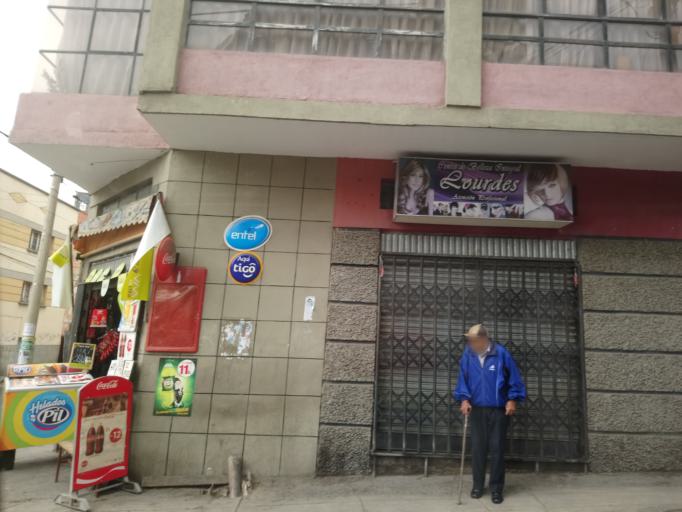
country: BO
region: La Paz
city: La Paz
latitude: -16.4916
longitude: -68.1523
